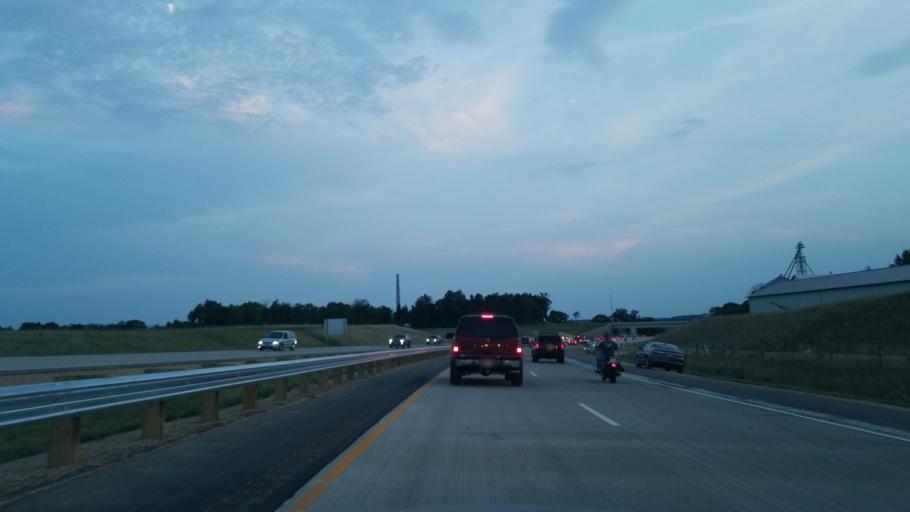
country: US
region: Minnesota
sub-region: Washington County
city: Oak Park Heights
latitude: 45.0504
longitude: -92.7788
